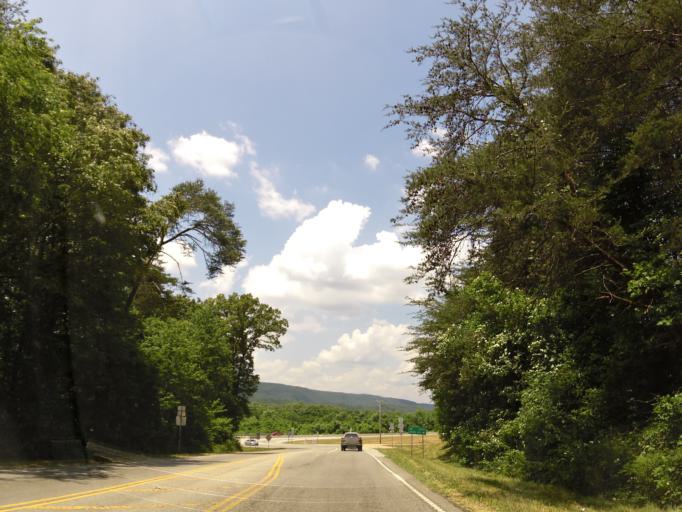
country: US
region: Tennessee
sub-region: Rhea County
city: Spring City
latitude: 35.6552
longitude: -84.8821
